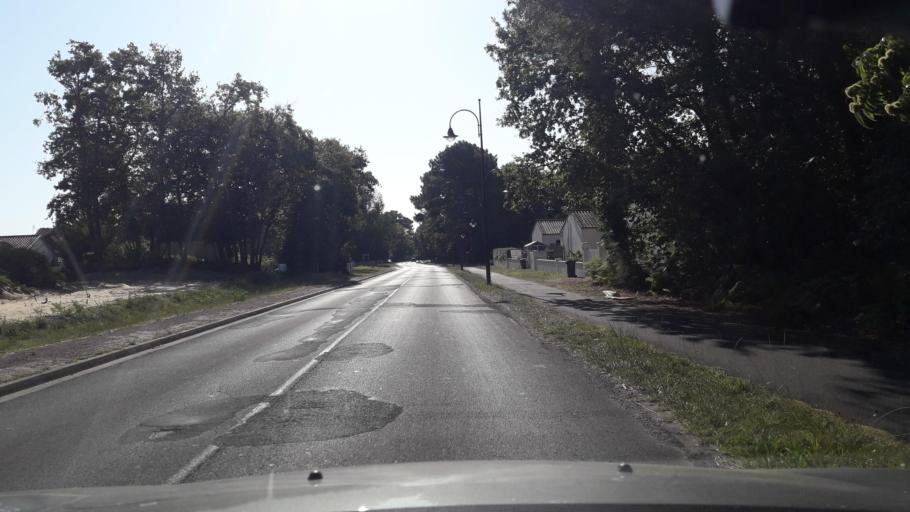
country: FR
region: Poitou-Charentes
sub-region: Departement de la Charente-Maritime
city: Les Mathes
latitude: 45.7144
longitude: -1.1436
